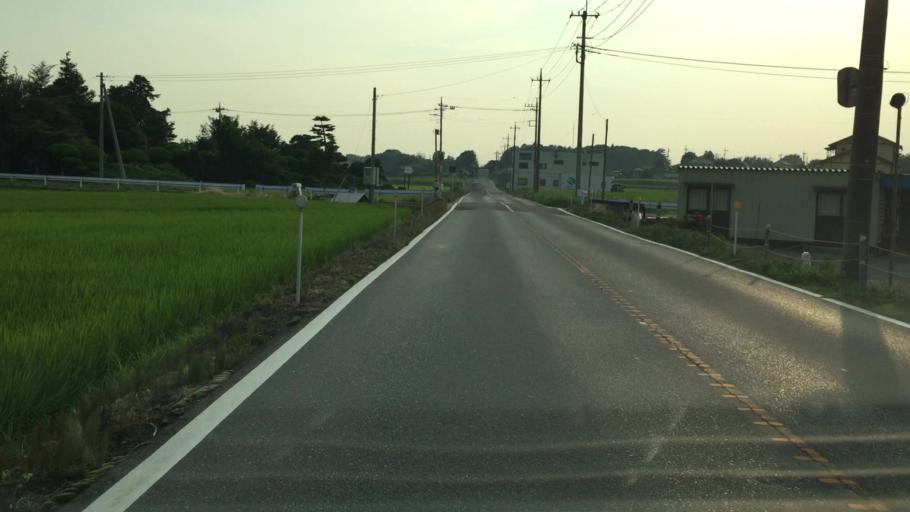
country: JP
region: Tochigi
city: Fujioka
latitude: 36.2614
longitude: 139.6320
